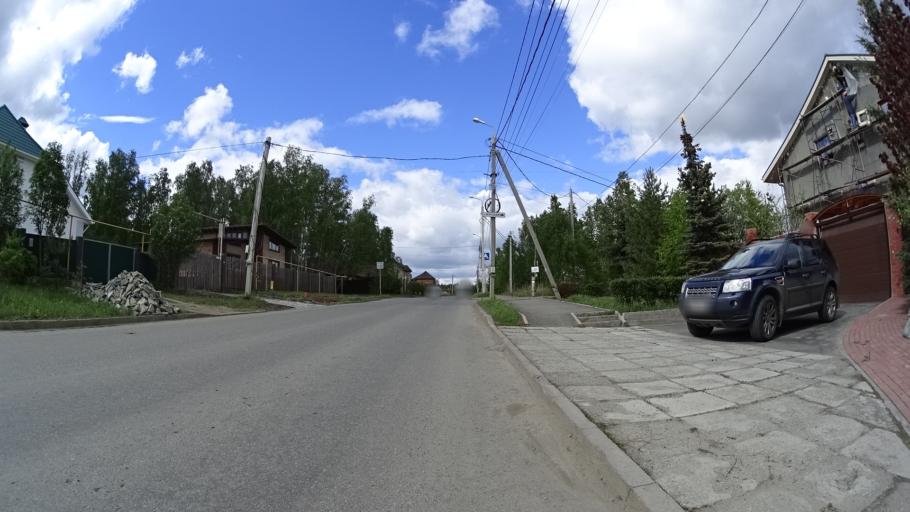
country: RU
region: Chelyabinsk
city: Sargazy
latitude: 55.1575
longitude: 61.2519
